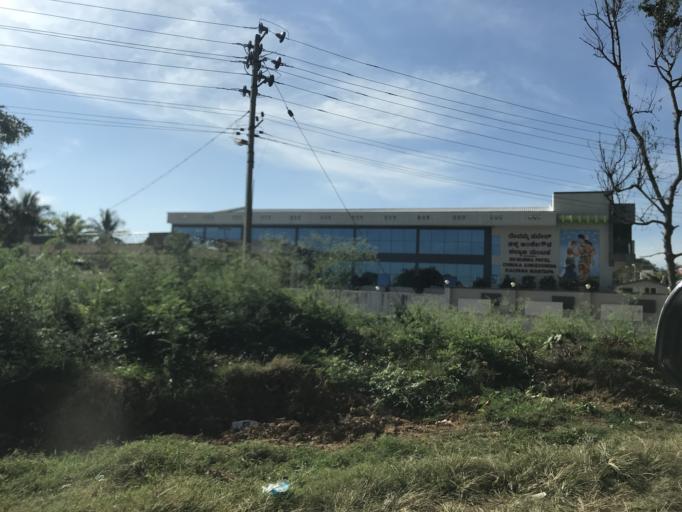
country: IN
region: Karnataka
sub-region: Mysore
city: Mysore
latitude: 12.2078
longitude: 76.5563
